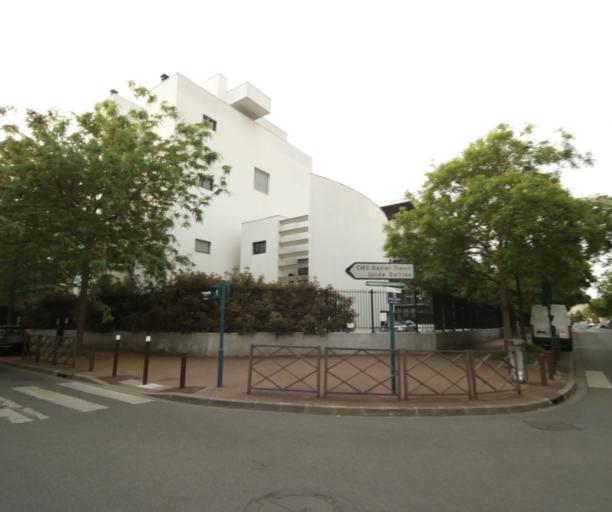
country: FR
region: Ile-de-France
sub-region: Departement des Hauts-de-Seine
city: Gennevilliers
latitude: 48.9200
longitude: 2.3042
